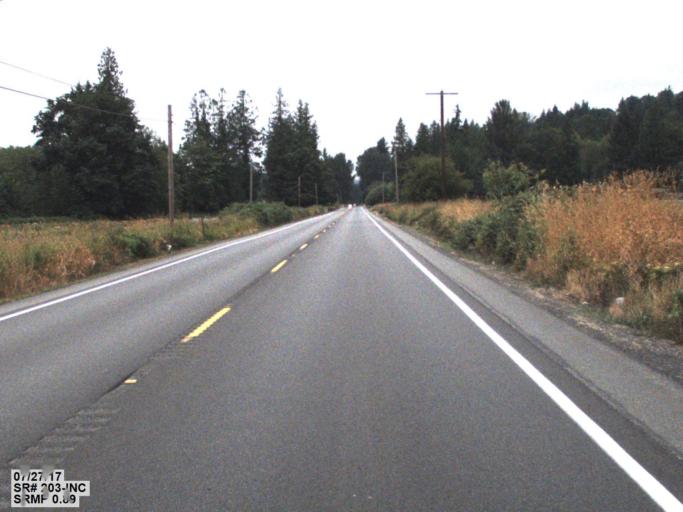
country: US
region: Washington
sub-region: King County
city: Fall City
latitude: 47.5803
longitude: -121.8953
